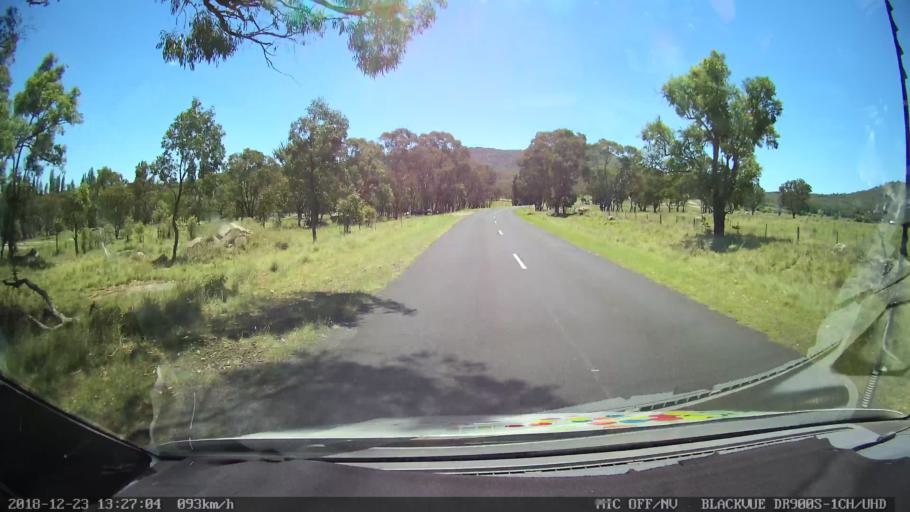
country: AU
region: New South Wales
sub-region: Armidale Dumaresq
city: Armidale
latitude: -30.4636
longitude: 151.3604
